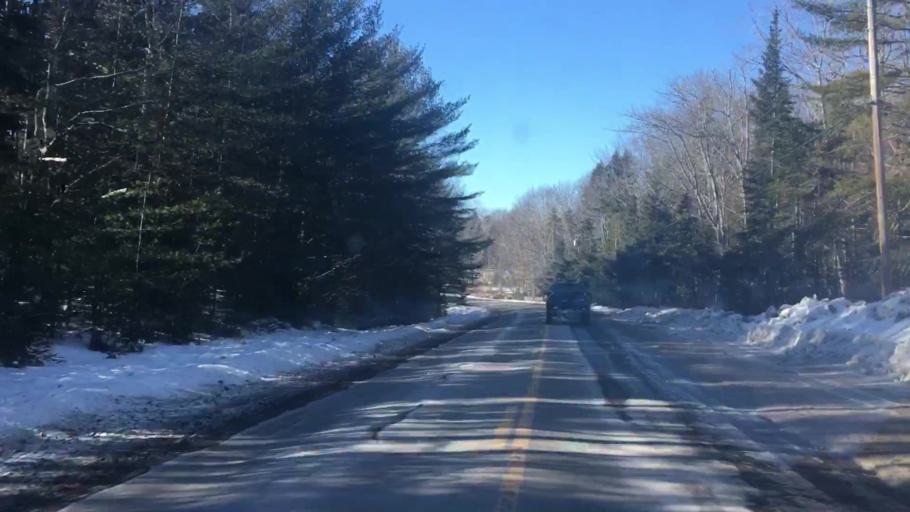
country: US
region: Maine
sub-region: Hancock County
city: Sedgwick
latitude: 44.3979
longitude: -68.6309
